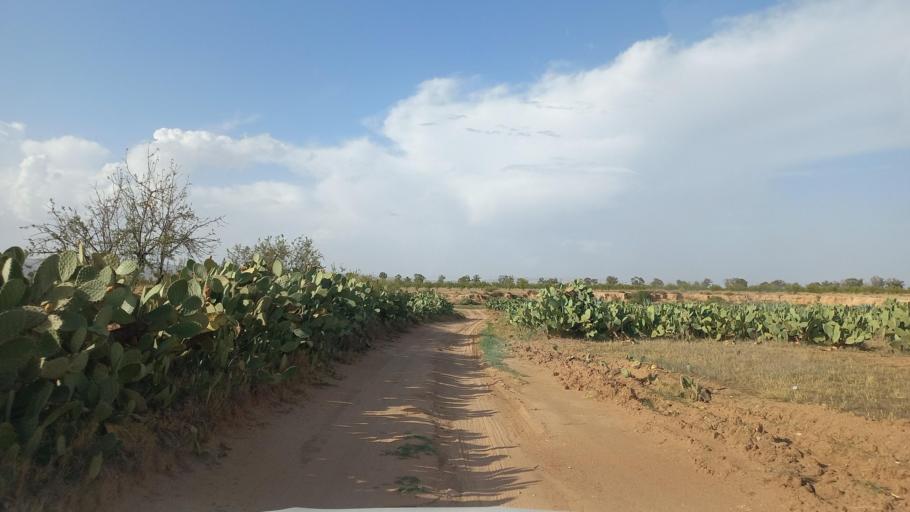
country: TN
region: Al Qasrayn
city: Kasserine
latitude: 35.2275
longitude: 8.9678
